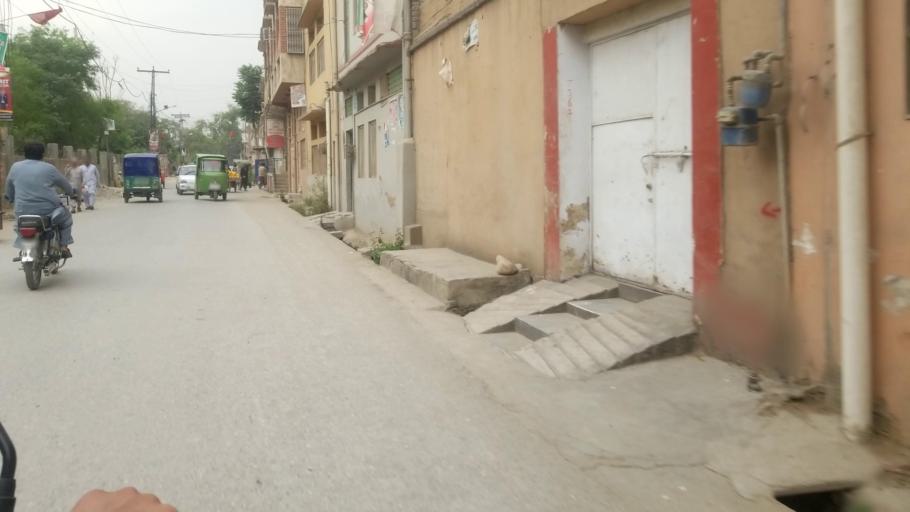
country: PK
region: Khyber Pakhtunkhwa
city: Peshawar
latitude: 33.9977
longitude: 71.5644
